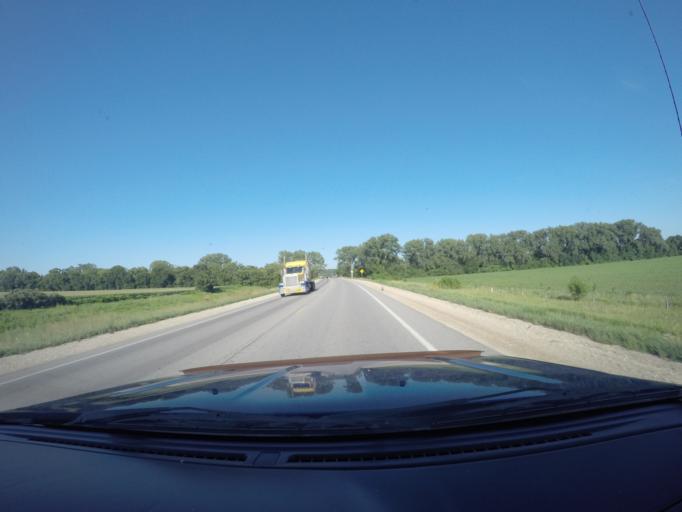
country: US
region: Kansas
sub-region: Jefferson County
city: Oskaloosa
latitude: 39.0807
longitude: -95.3997
